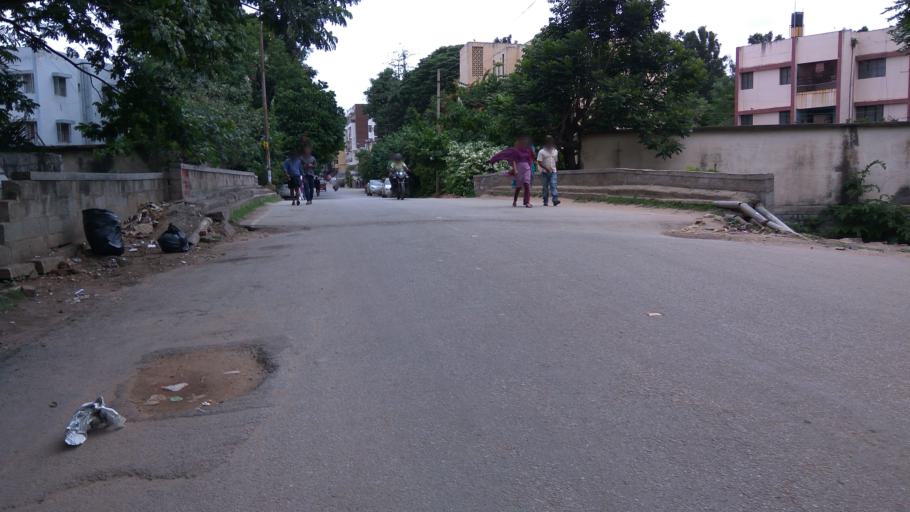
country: IN
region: Karnataka
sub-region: Bangalore Urban
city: Bangalore
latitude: 12.9633
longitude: 77.6382
